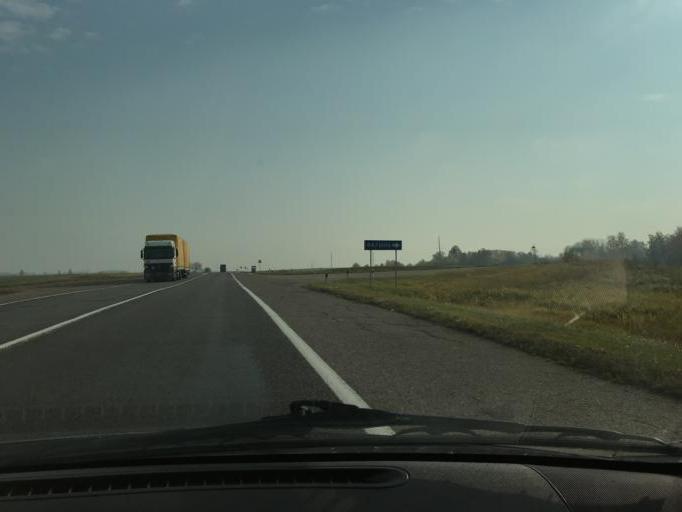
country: BY
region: Vitebsk
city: Chashniki
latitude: 55.0162
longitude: 29.0447
